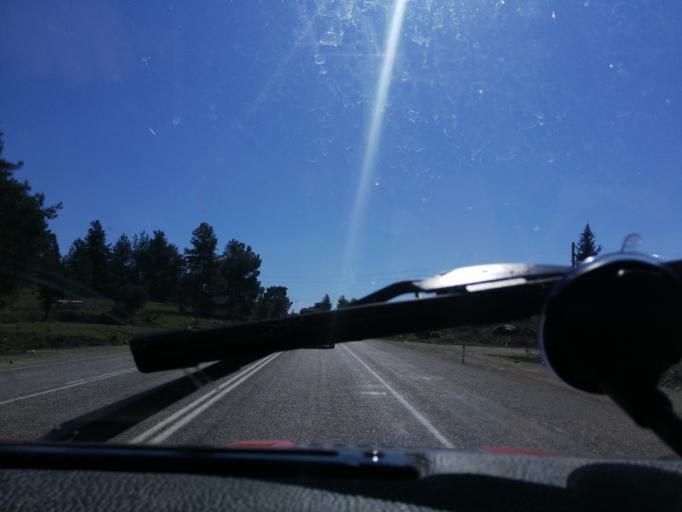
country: TR
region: Mugla
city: Kemer
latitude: 36.6111
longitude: 29.3583
